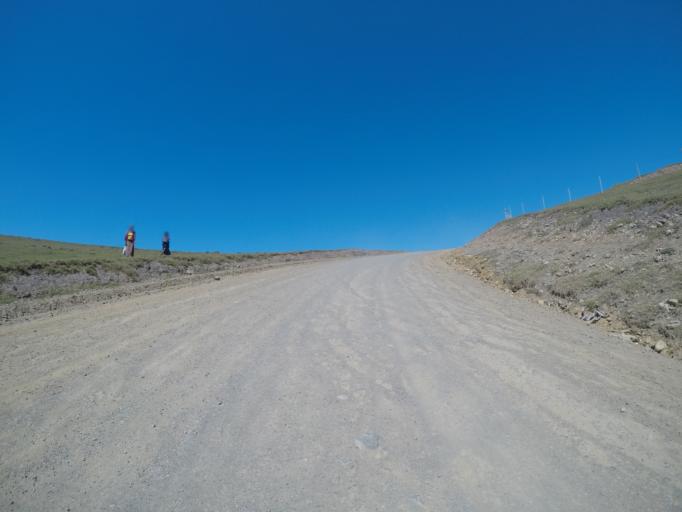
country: ZA
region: Eastern Cape
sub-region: OR Tambo District Municipality
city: Libode
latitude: -31.9905
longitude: 29.1448
